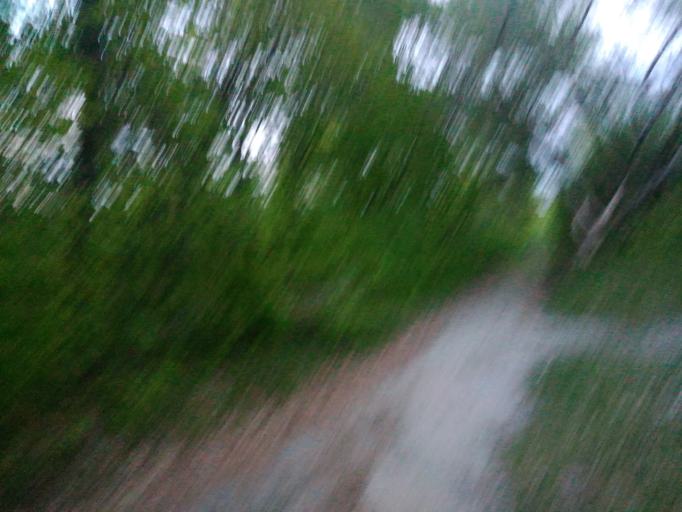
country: RU
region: Ulyanovsk
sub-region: Ulyanovskiy Rayon
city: Ulyanovsk
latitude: 54.2750
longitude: 48.3561
